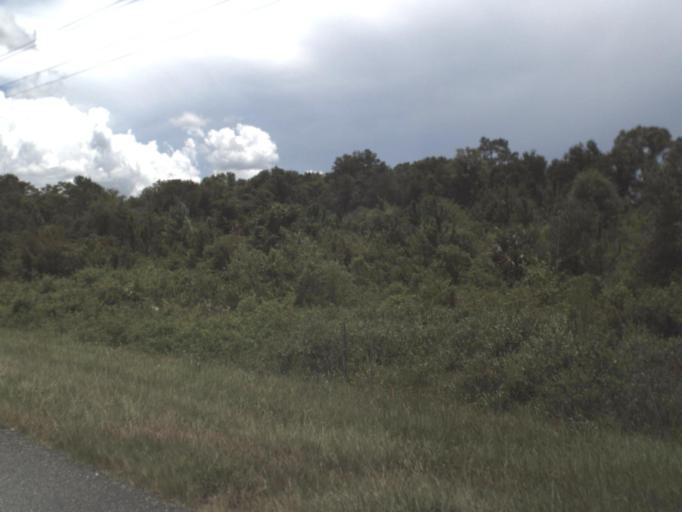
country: US
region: Florida
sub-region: Taylor County
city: Perry
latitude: 30.1428
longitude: -83.8604
